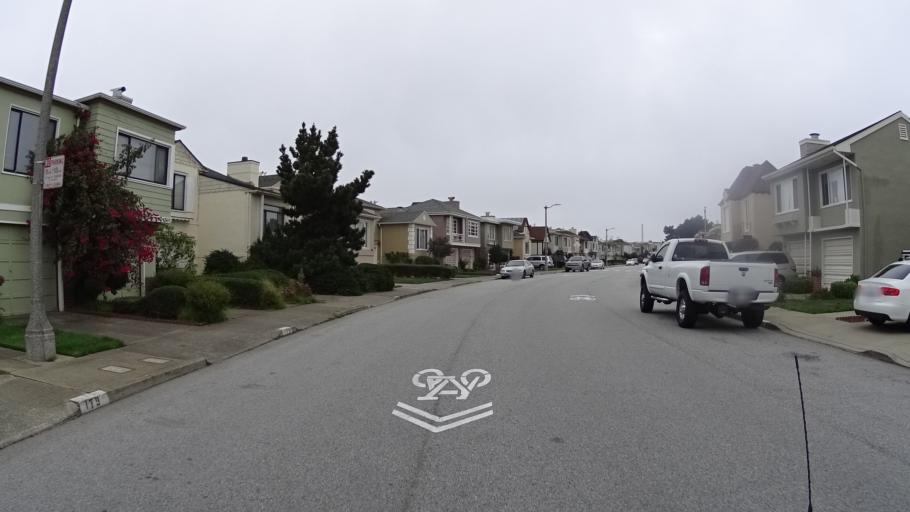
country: US
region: California
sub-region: San Mateo County
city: Daly City
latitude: 37.7302
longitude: -122.4913
